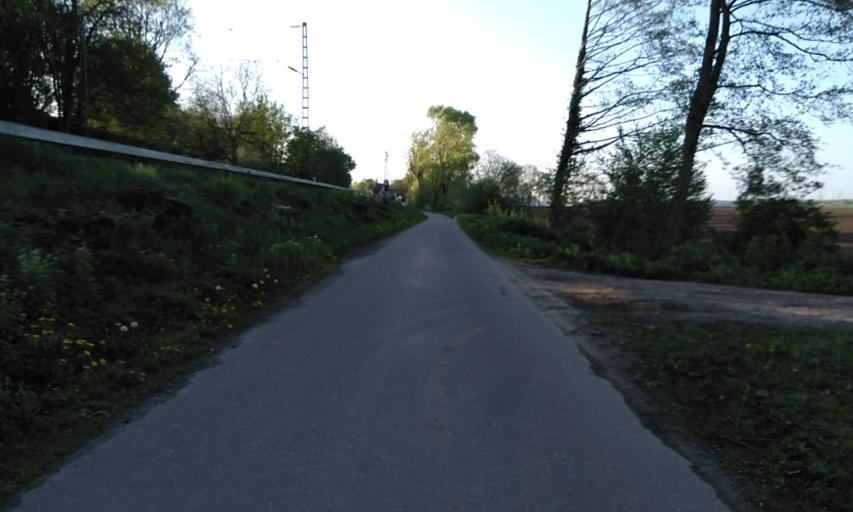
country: DE
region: Lower Saxony
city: Dollern
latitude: 53.5423
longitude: 9.5604
